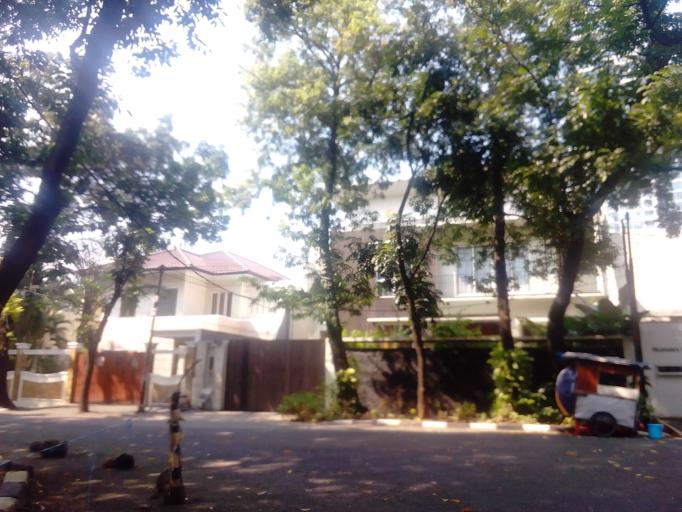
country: ID
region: Jakarta Raya
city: Jakarta
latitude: -6.2561
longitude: 106.8059
